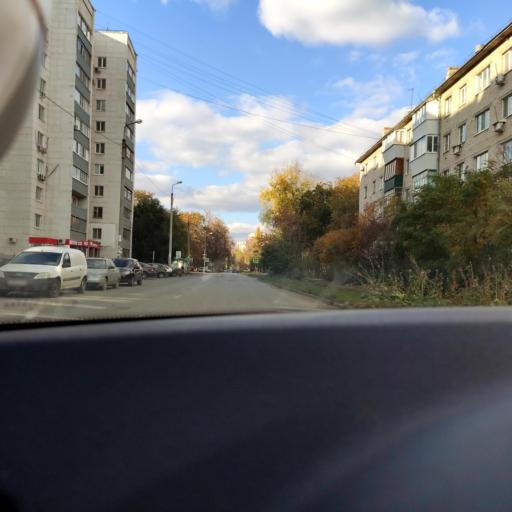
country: RU
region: Samara
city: Petra-Dubrava
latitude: 53.2281
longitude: 50.2755
